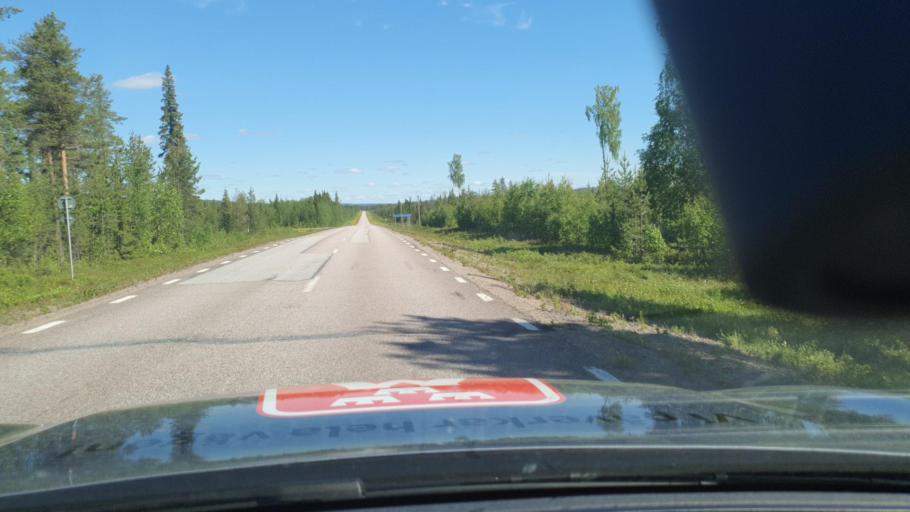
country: SE
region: Norrbotten
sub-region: Overkalix Kommun
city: OEverkalix
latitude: 66.8667
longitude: 22.7559
